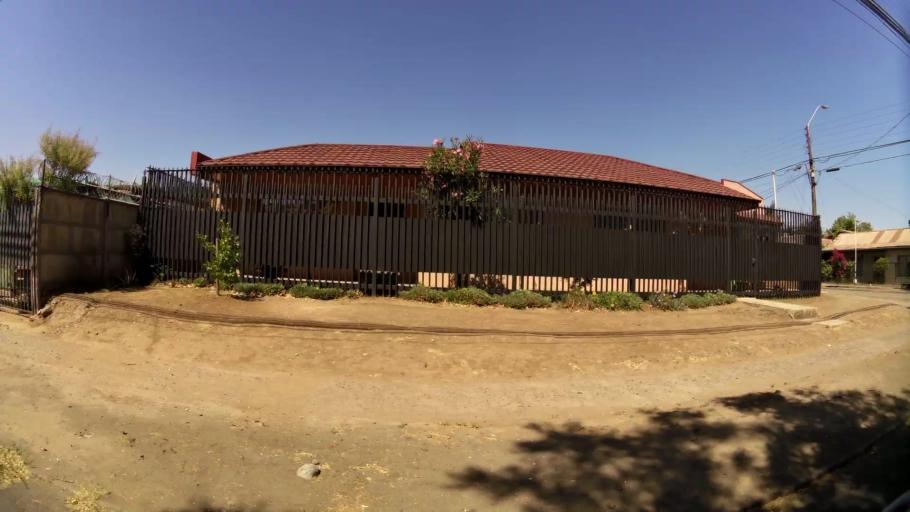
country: CL
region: Maule
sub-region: Provincia de Talca
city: Talca
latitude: -35.4144
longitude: -71.6574
